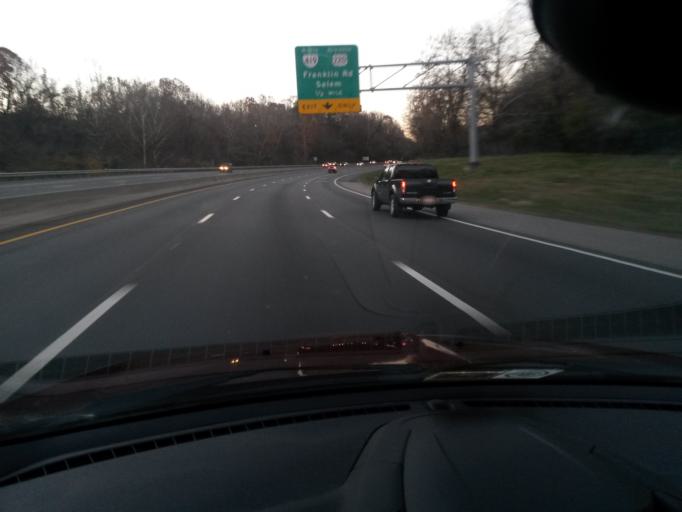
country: US
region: Virginia
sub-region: Roanoke County
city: Narrows
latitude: 37.2409
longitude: -79.9722
